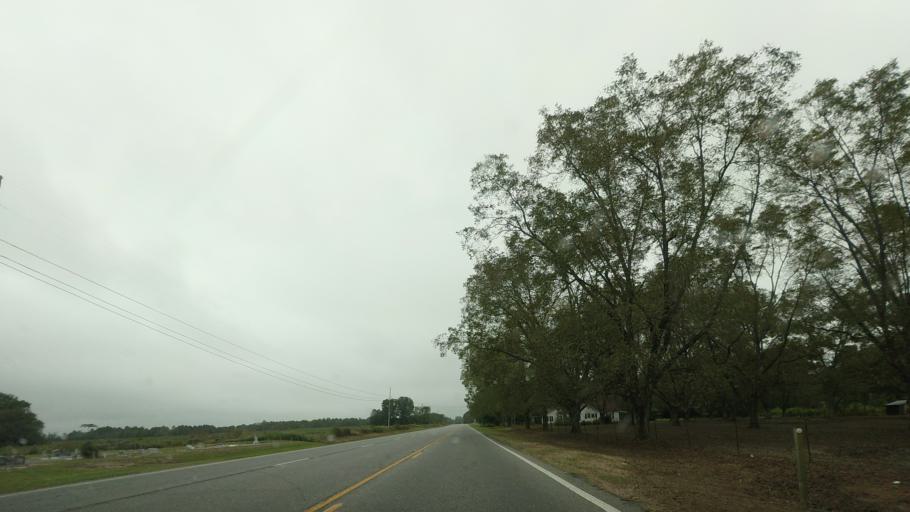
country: US
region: Georgia
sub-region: Ben Hill County
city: Fitzgerald
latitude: 31.6708
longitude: -83.2354
